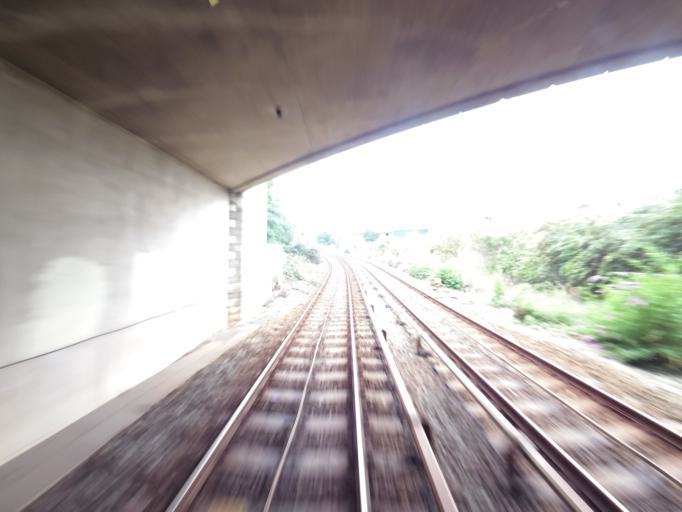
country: GB
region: England
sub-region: Greater London
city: Poplar
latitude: 51.5095
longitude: 0.0108
